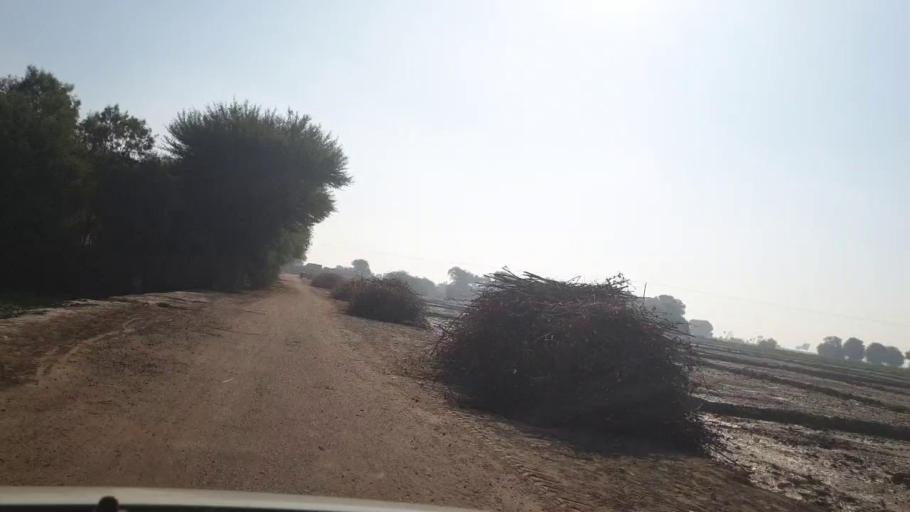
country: PK
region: Sindh
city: Dadu
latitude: 26.6375
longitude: 67.8340
